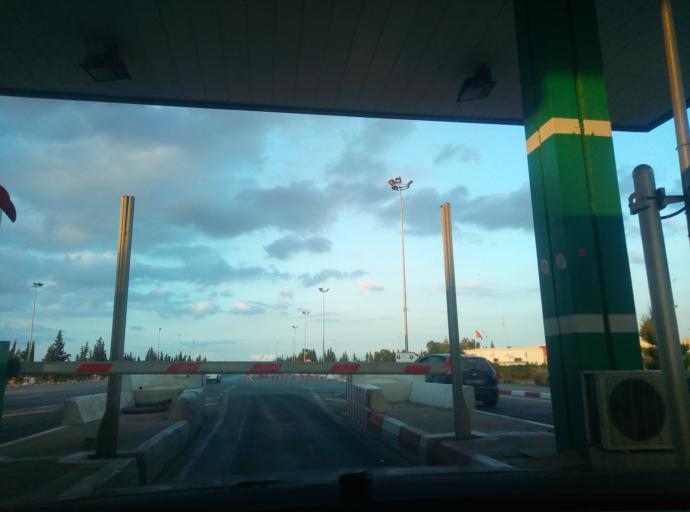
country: TN
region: Tunis
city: Oued Lill
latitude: 36.7129
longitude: 9.9738
